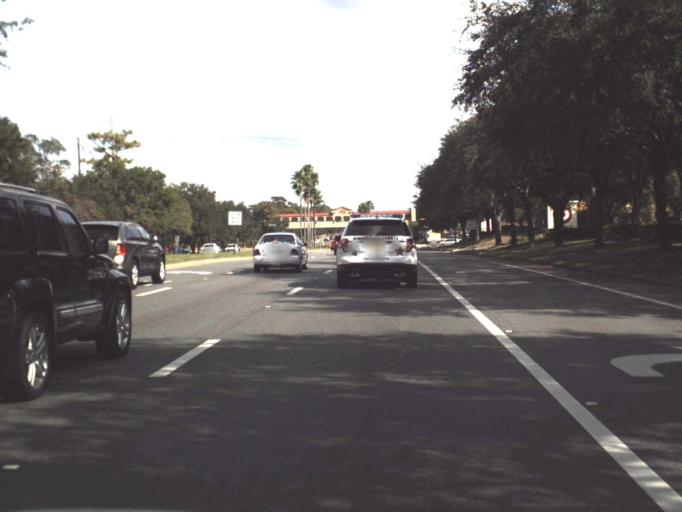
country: US
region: Florida
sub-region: Seminole County
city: Heathrow
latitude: 28.7560
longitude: -81.3496
